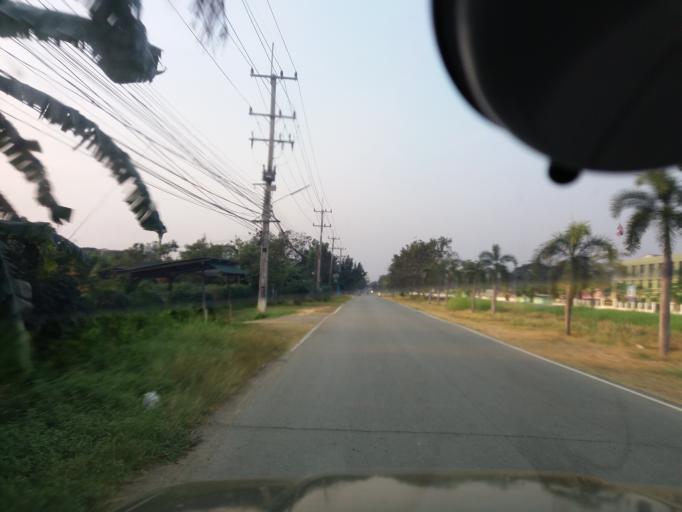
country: TH
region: Sing Buri
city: Sing Buri
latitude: 14.8793
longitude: 100.4034
